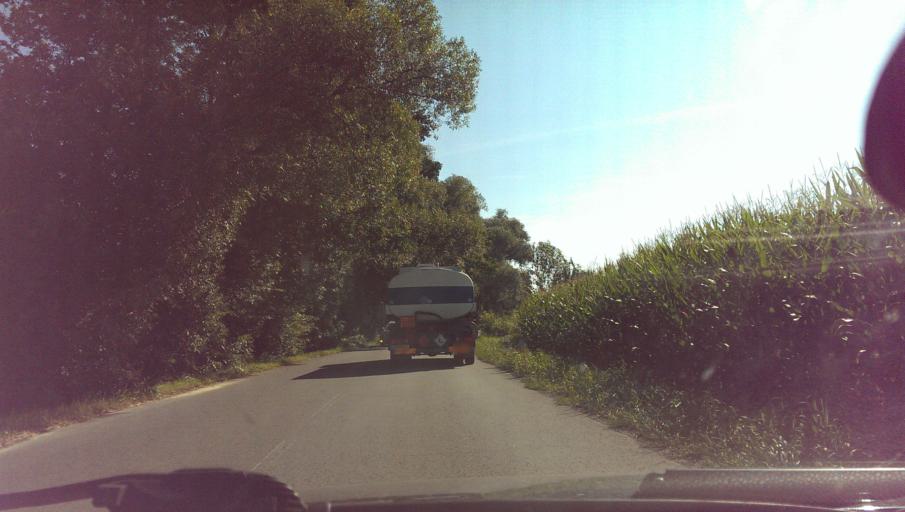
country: CZ
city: Frycovice
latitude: 49.6821
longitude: 18.2344
